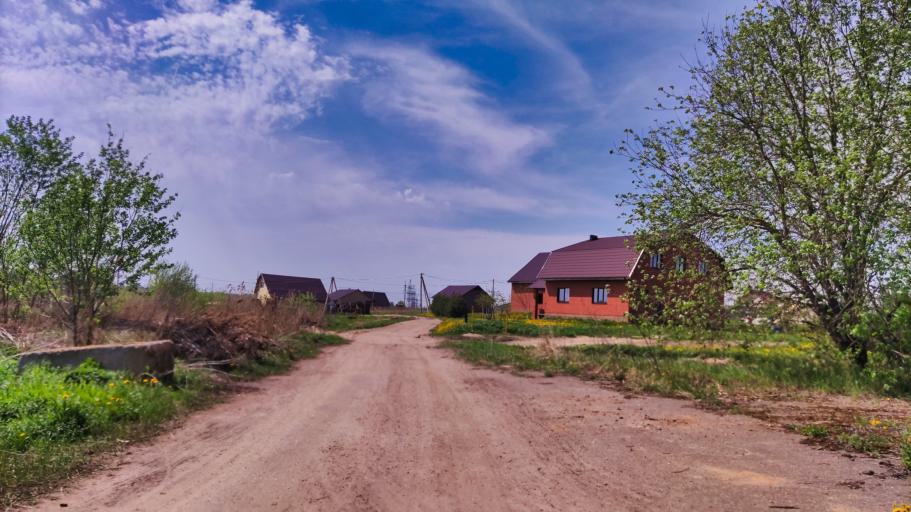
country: RU
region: Tverskaya
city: Rzhev
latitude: 56.2353
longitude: 34.3283
